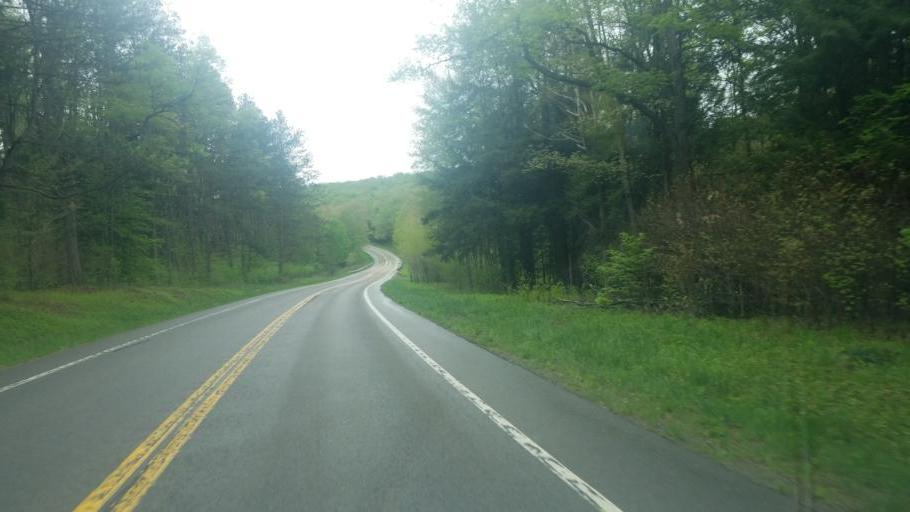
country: US
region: Pennsylvania
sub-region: Forest County
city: Marienville
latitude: 41.5504
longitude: -79.0158
